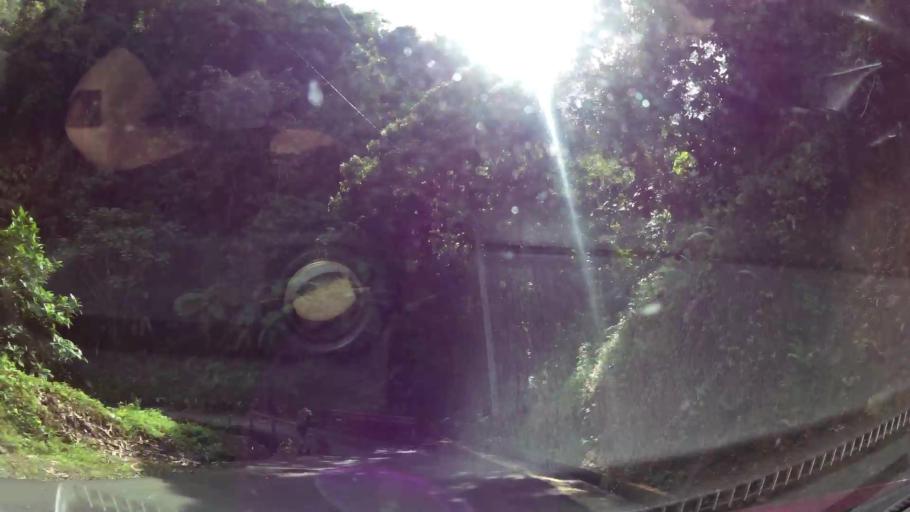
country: DM
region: Saint John
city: Portsmouth
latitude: 15.6253
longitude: -61.4261
